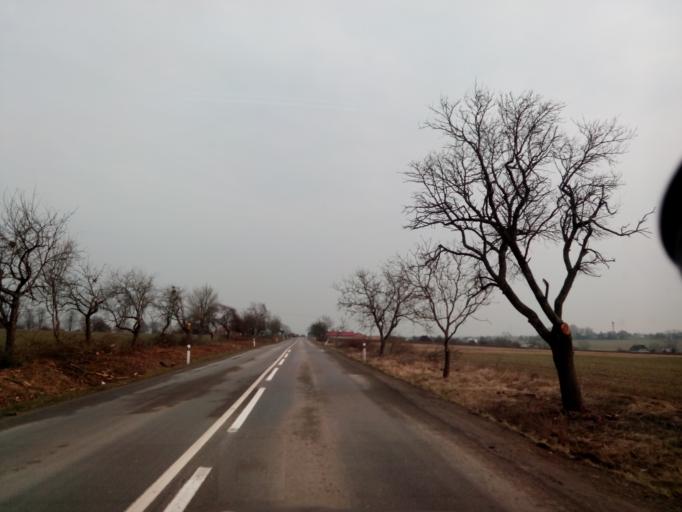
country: SK
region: Kosicky
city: Secovce
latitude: 48.6404
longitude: 21.5616
